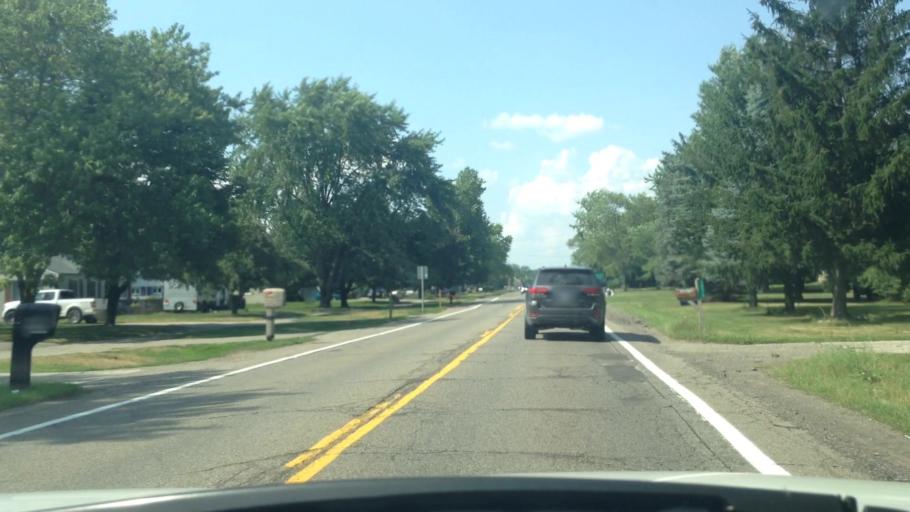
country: US
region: Michigan
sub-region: Oakland County
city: Waterford
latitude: 42.7158
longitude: -83.3787
